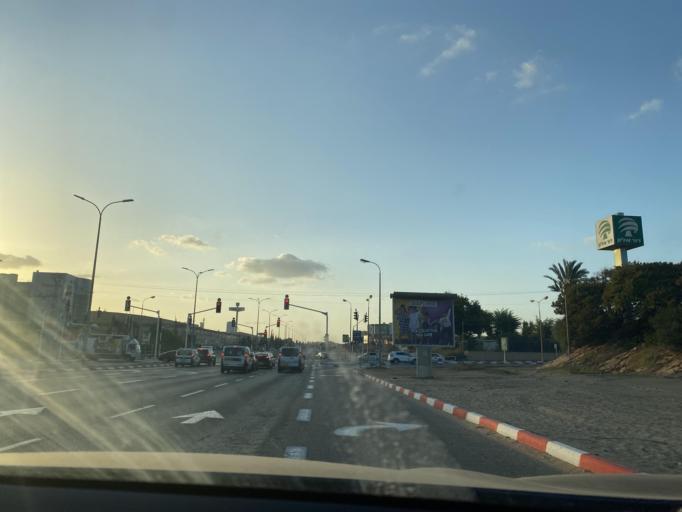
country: IL
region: Southern District
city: Ashdod
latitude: 31.8093
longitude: 34.6598
